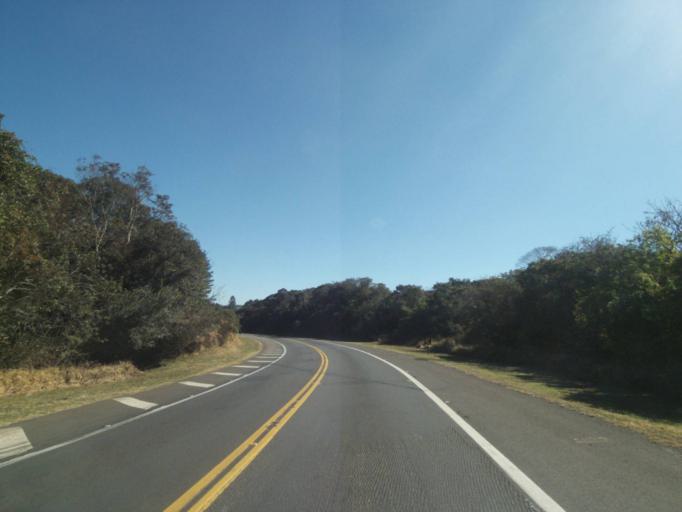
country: BR
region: Parana
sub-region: Tibagi
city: Tibagi
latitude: -24.6894
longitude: -50.5824
